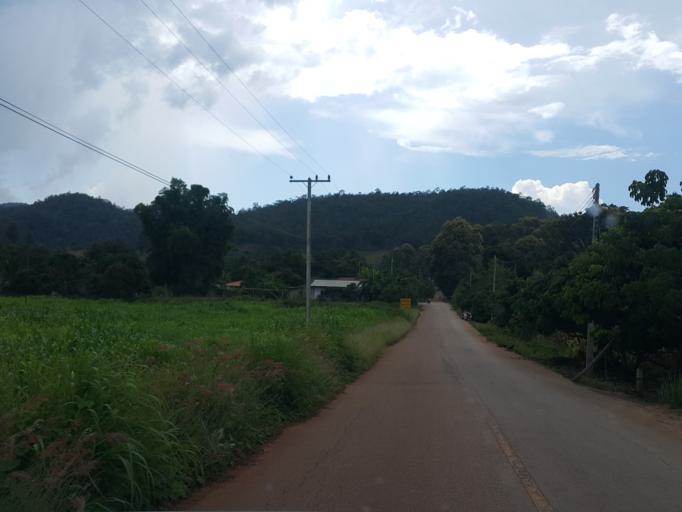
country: TH
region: Chiang Mai
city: Phrao
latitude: 19.3331
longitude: 99.1505
